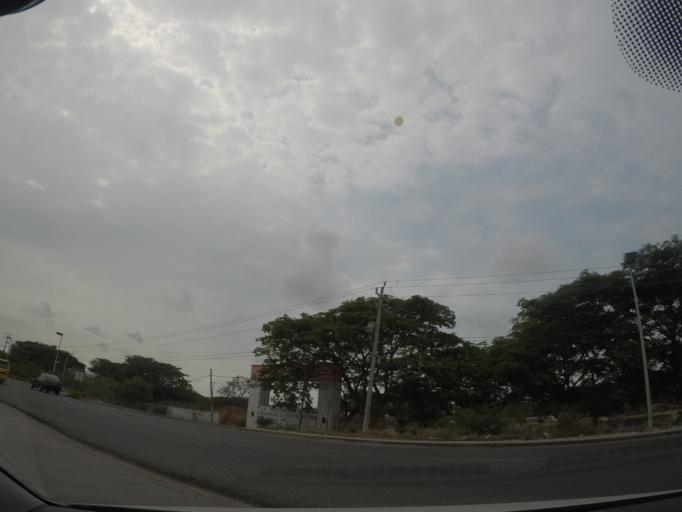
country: MX
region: Oaxaca
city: Juchitan de Zaragoza
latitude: 16.4476
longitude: -95.0146
